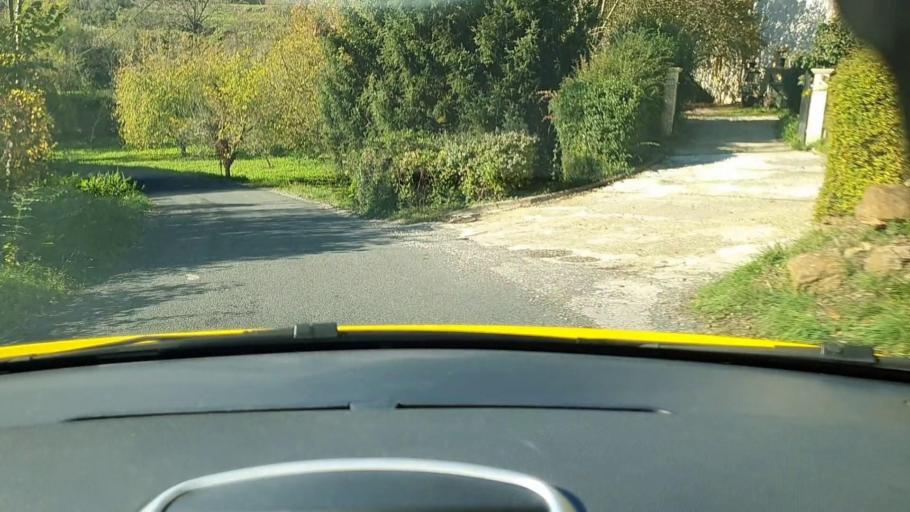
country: FR
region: Languedoc-Roussillon
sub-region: Departement du Gard
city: Le Vigan
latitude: 43.9956
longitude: 3.6247
